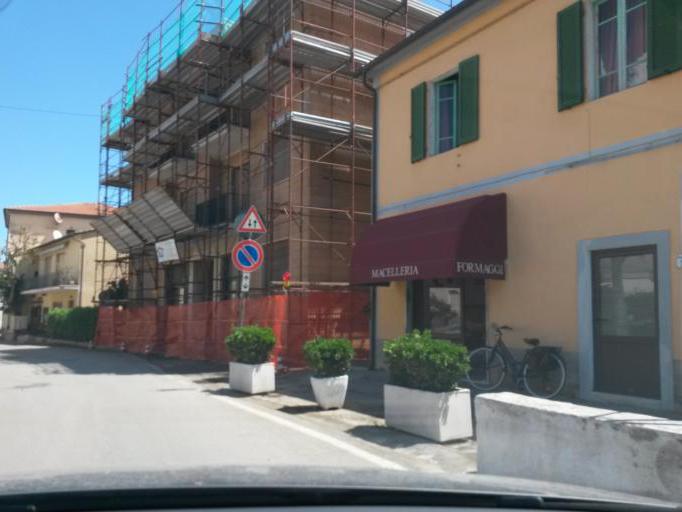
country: IT
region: Tuscany
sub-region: Provincia di Livorno
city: Rio Marina
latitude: 42.8590
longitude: 10.4205
